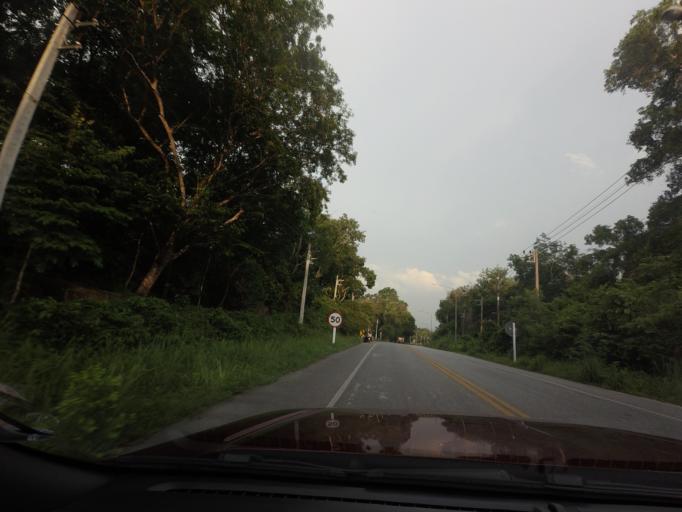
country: TH
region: Pattani
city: Mae Lan
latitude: 6.6681
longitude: 101.1609
